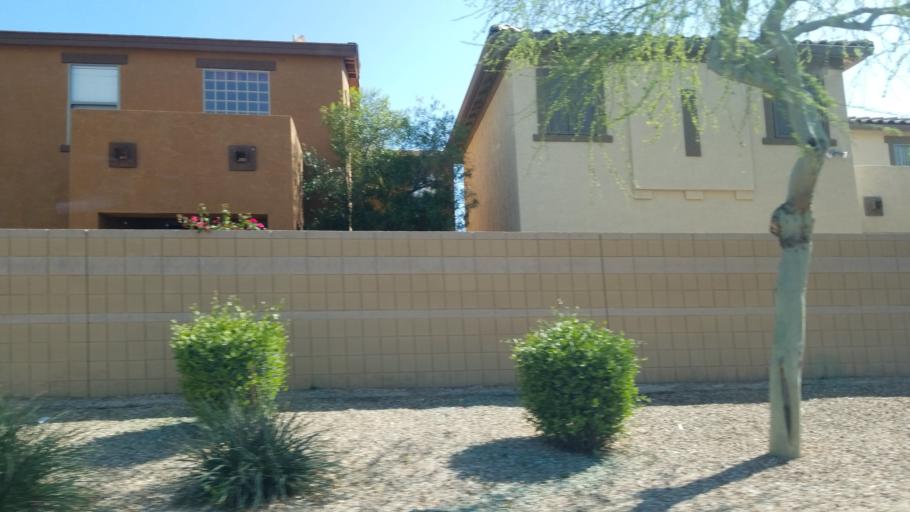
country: US
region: Arizona
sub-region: Maricopa County
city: Glendale
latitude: 33.5637
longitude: -112.1967
